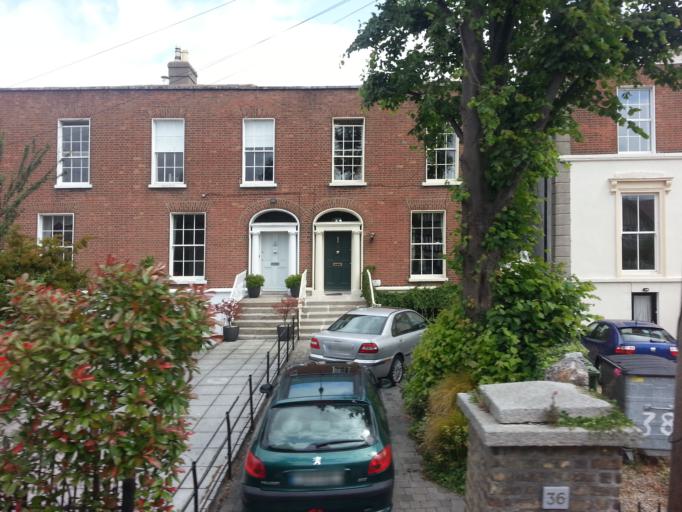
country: IE
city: Milltown
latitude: 53.3226
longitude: -6.2482
